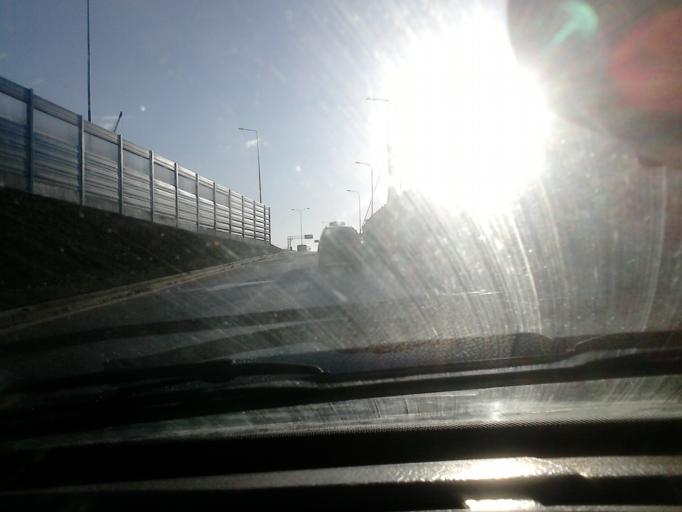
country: PL
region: Pomeranian Voivodeship
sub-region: Gdansk
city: Gdansk
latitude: 54.3596
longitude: 18.6917
